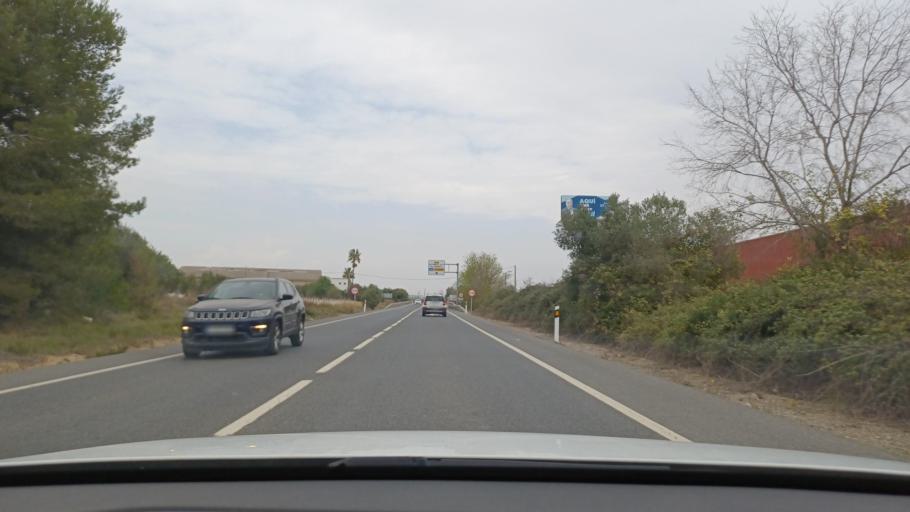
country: ES
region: Catalonia
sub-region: Provincia de Tarragona
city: la Pobla de Mafumet
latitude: 41.1828
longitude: 1.2415
